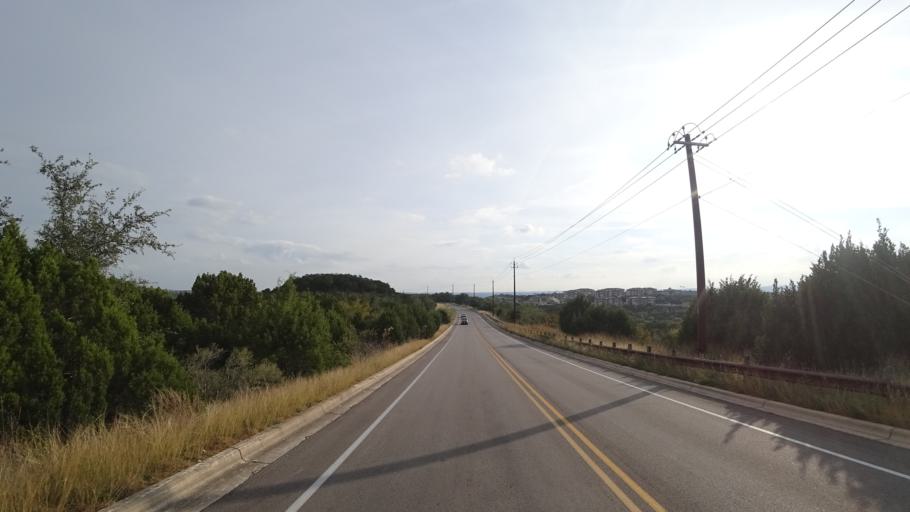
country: US
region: Texas
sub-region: Travis County
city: Hudson Bend
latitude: 30.3890
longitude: -97.8707
